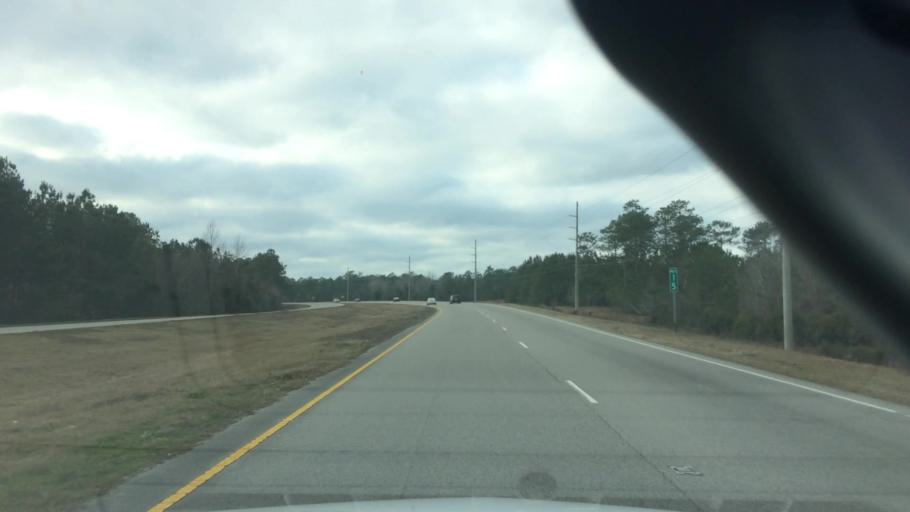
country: US
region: North Carolina
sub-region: Brunswick County
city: Shallotte
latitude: 33.9893
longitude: -78.3817
